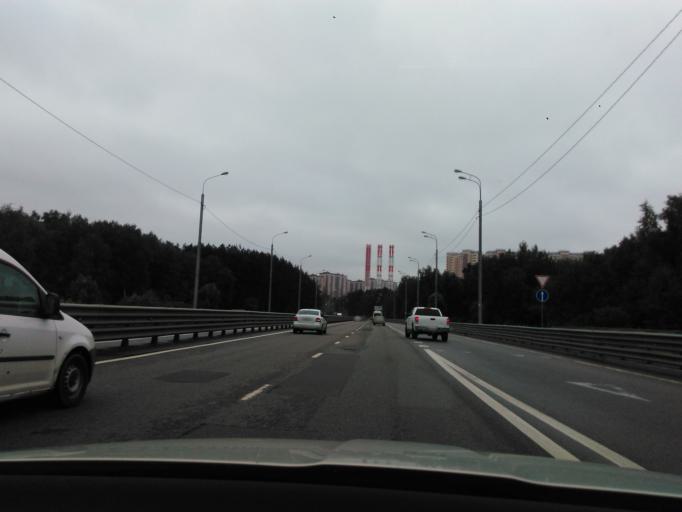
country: RU
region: Moscow
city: Khimki
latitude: 55.8810
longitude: 37.4056
